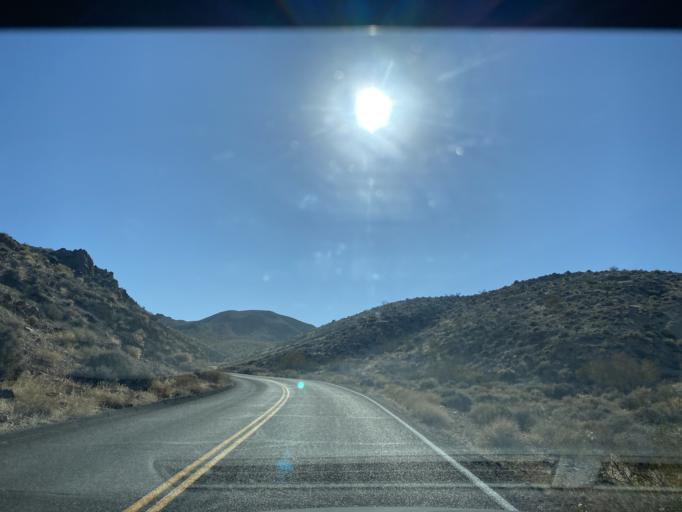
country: US
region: Nevada
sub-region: Nye County
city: Beatty
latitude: 36.2343
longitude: -116.6971
